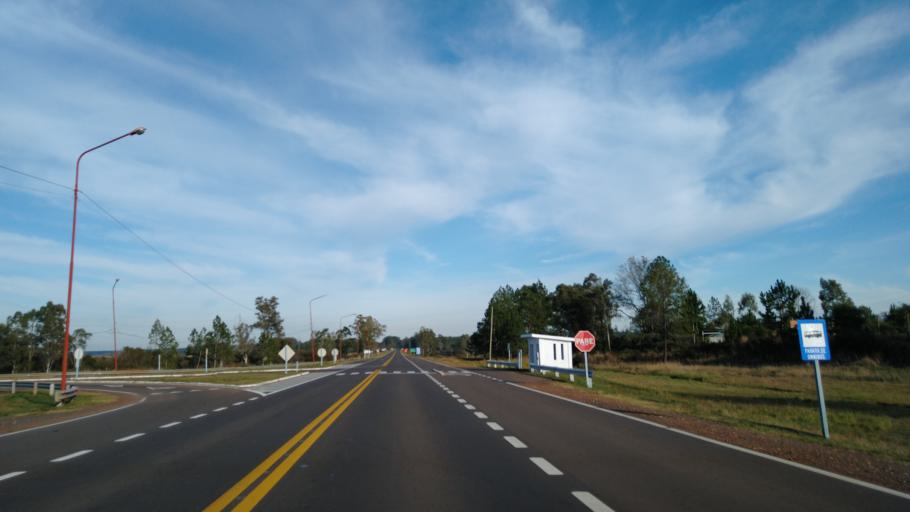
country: AR
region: Corrientes
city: Yapeyu
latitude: -29.4221
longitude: -56.8453
